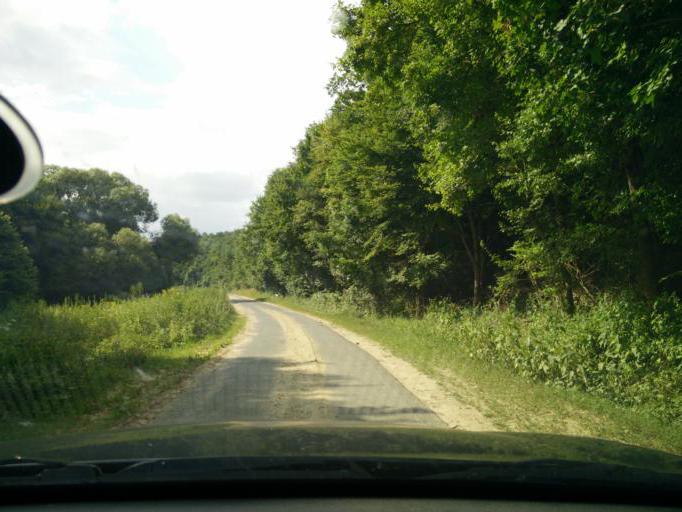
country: HU
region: Komarom-Esztergom
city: Sutto
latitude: 47.7133
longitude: 18.4574
